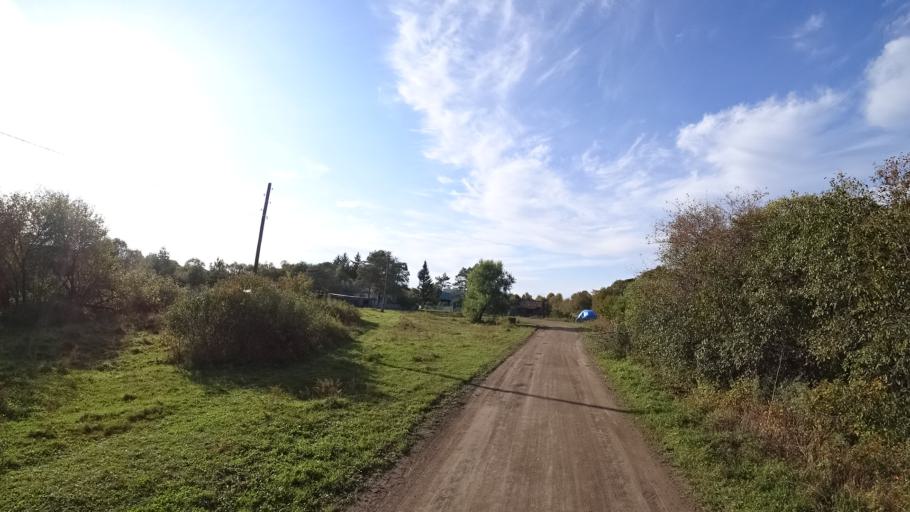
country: RU
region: Amur
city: Arkhara
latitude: 49.3505
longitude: 130.1142
